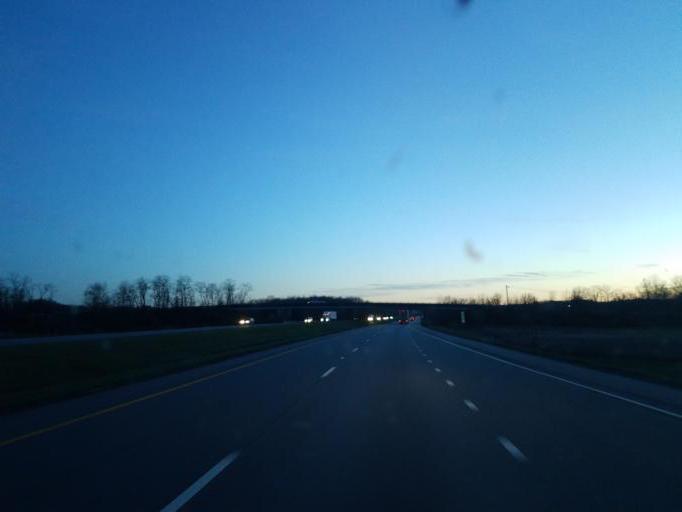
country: US
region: Ohio
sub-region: Muskingum County
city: New Concord
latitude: 39.9904
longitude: -81.6746
